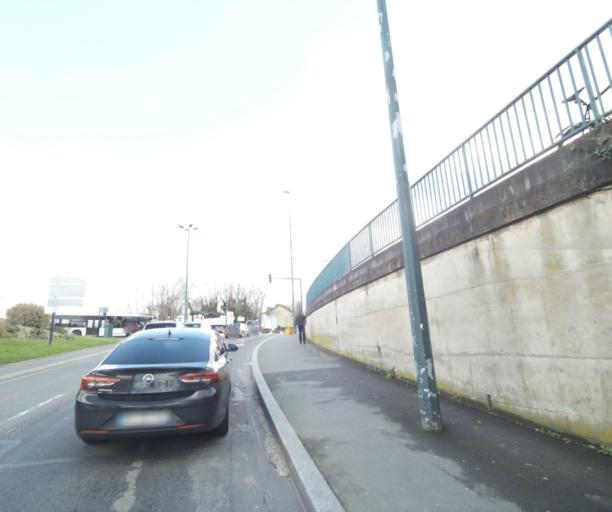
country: FR
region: Ile-de-France
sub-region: Departement de Seine-Saint-Denis
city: Villetaneuse
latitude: 48.9587
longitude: 2.3285
